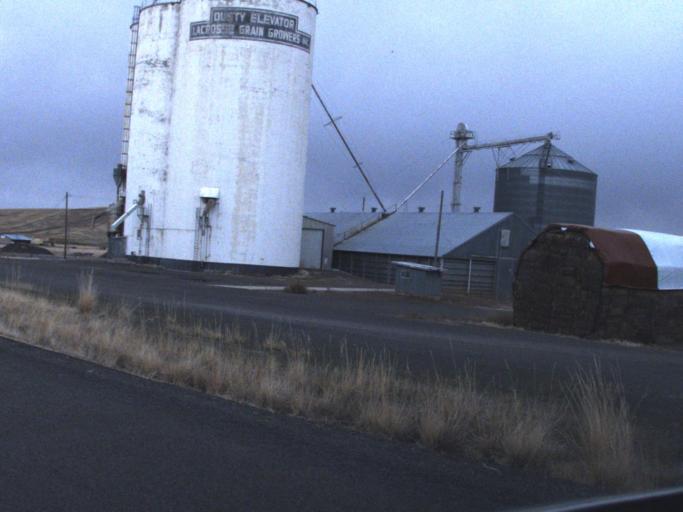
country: US
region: Washington
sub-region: Whitman County
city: Colfax
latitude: 46.8107
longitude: -117.6396
